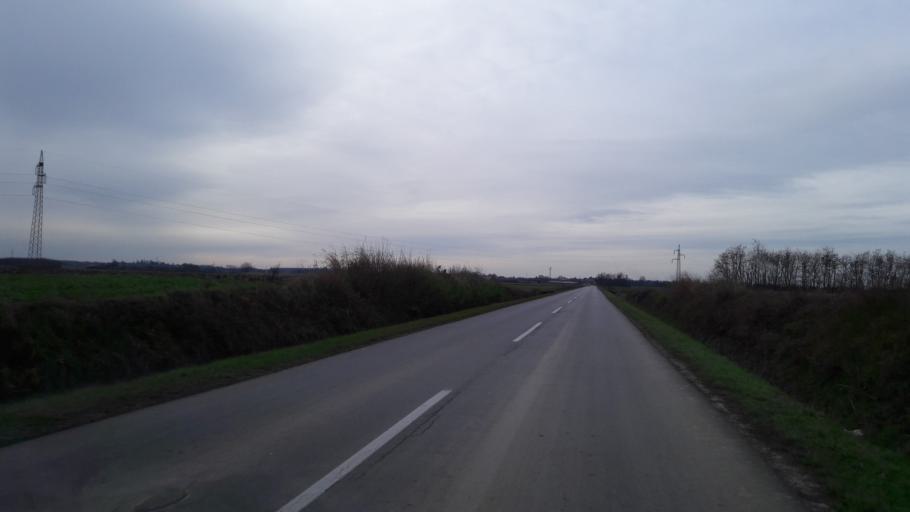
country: HR
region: Osjecko-Baranjska
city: Semeljci
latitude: 45.3770
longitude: 18.5568
